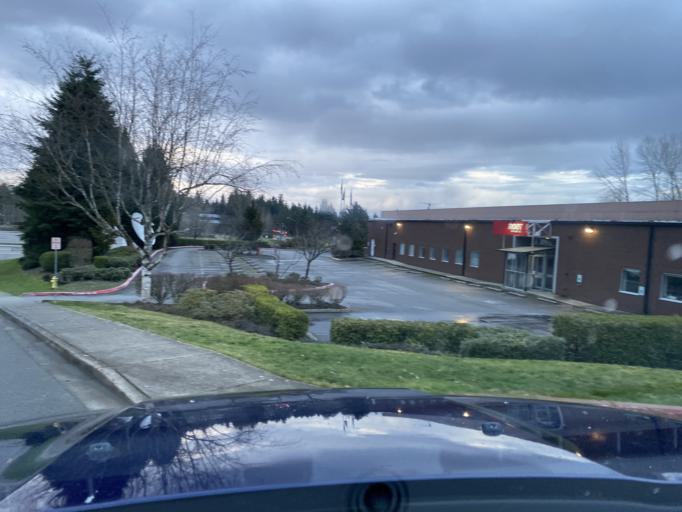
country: US
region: Washington
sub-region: King County
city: Eastgate
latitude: 47.5766
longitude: -122.1321
